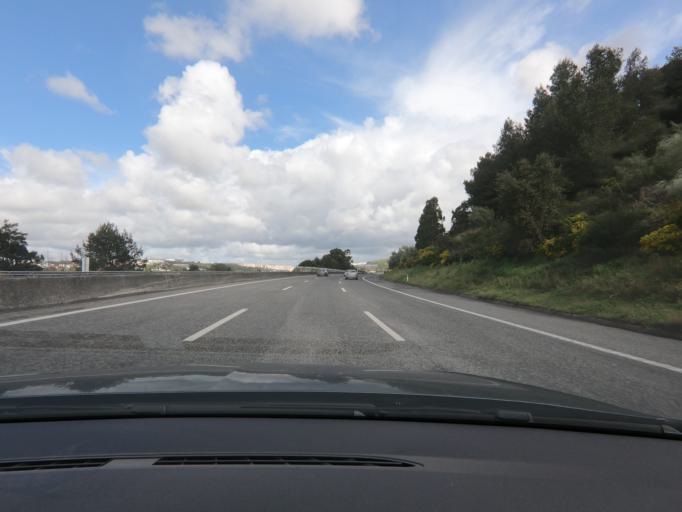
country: PT
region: Lisbon
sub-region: Oeiras
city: Quejas
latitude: 38.7220
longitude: -9.2729
